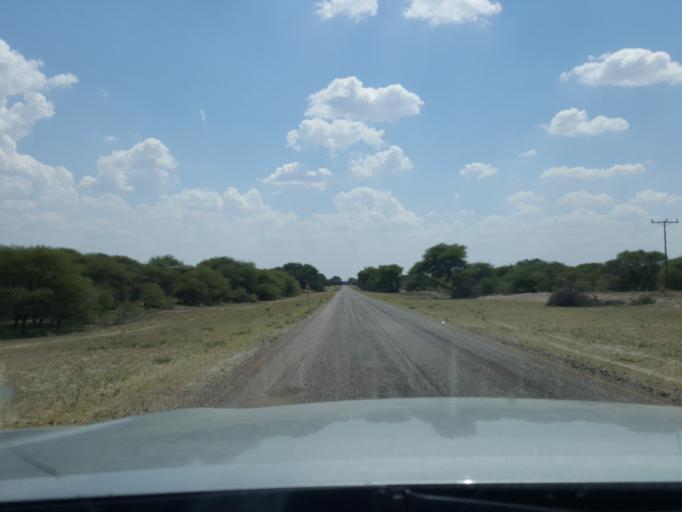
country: BW
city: Tsau
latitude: -20.1856
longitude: 22.4713
